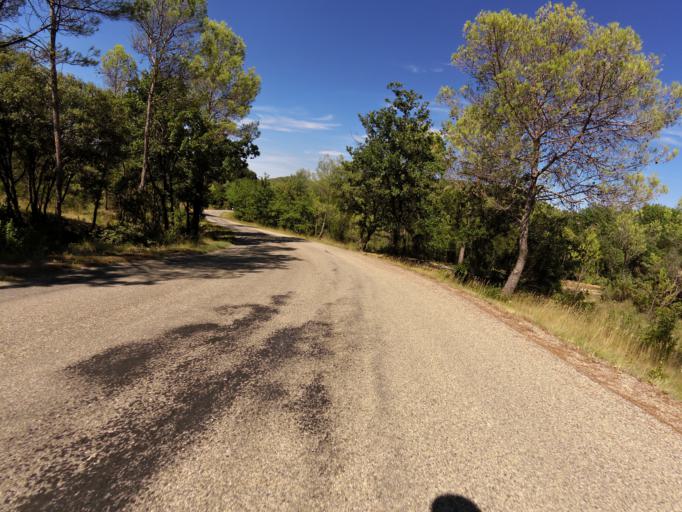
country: FR
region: Languedoc-Roussillon
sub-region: Departement du Gard
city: Quissac
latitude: 43.9070
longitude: 4.0460
